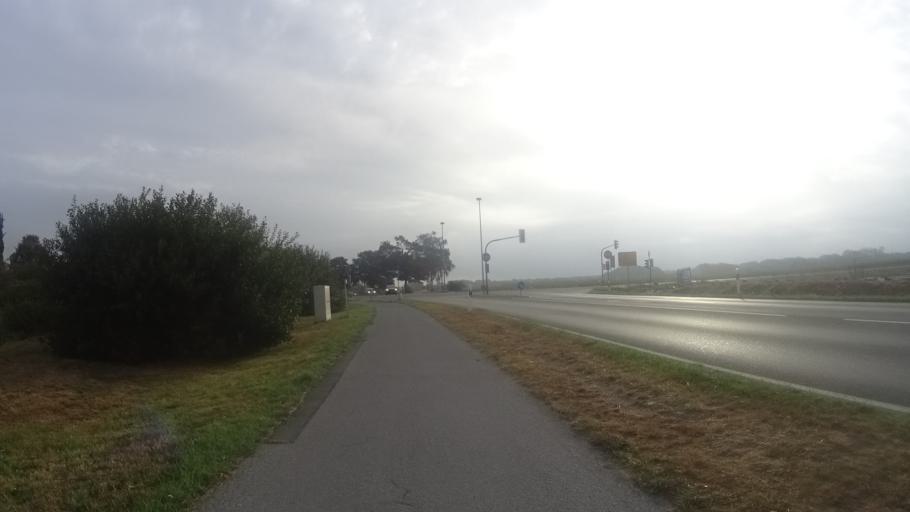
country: DE
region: North Rhine-Westphalia
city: Straelen
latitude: 51.4998
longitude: 6.2494
